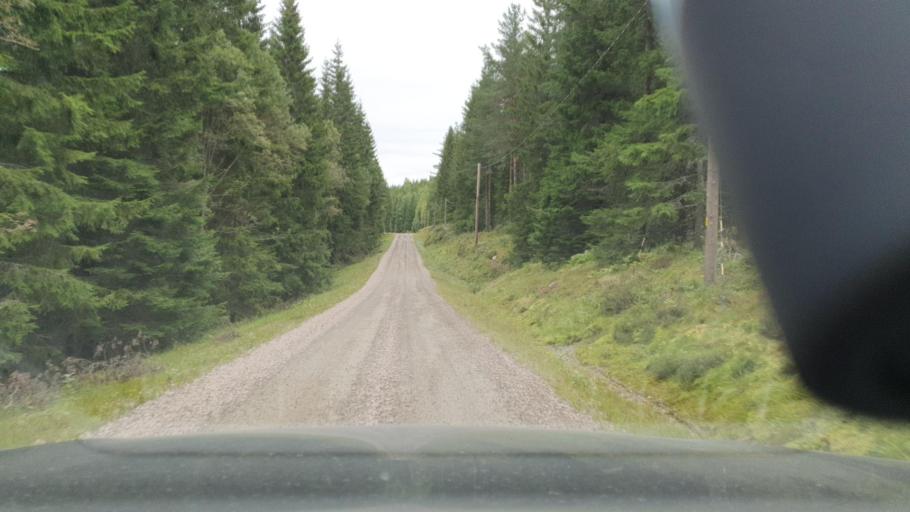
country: SE
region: Vaermland
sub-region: Eda Kommun
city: Charlottenberg
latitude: 60.1364
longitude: 12.5933
